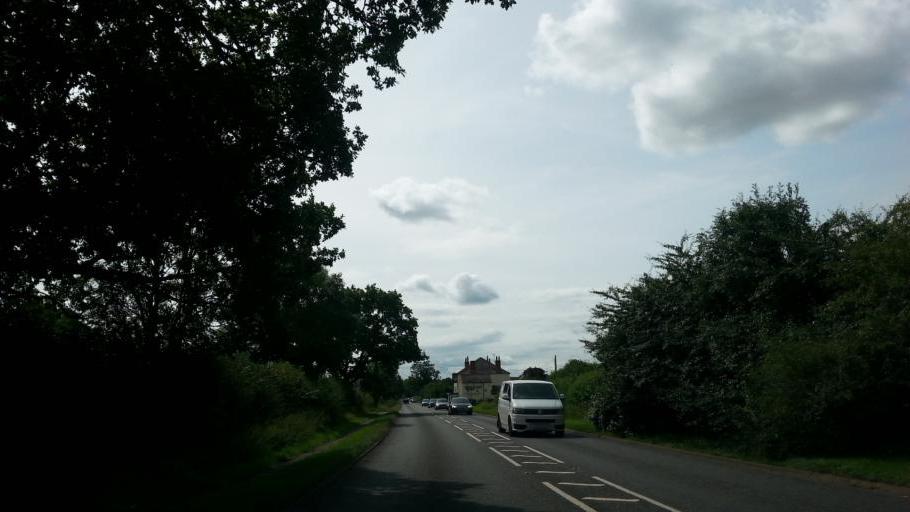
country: GB
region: England
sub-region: Leicestershire
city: Blaby
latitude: 52.5597
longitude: -1.1709
